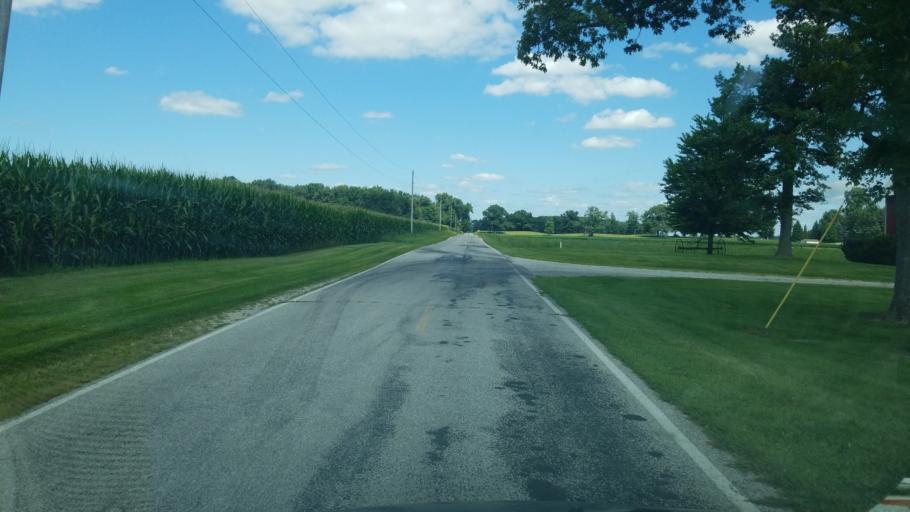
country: US
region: Ohio
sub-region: Fulton County
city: Delta
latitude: 41.6231
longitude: -84.0152
